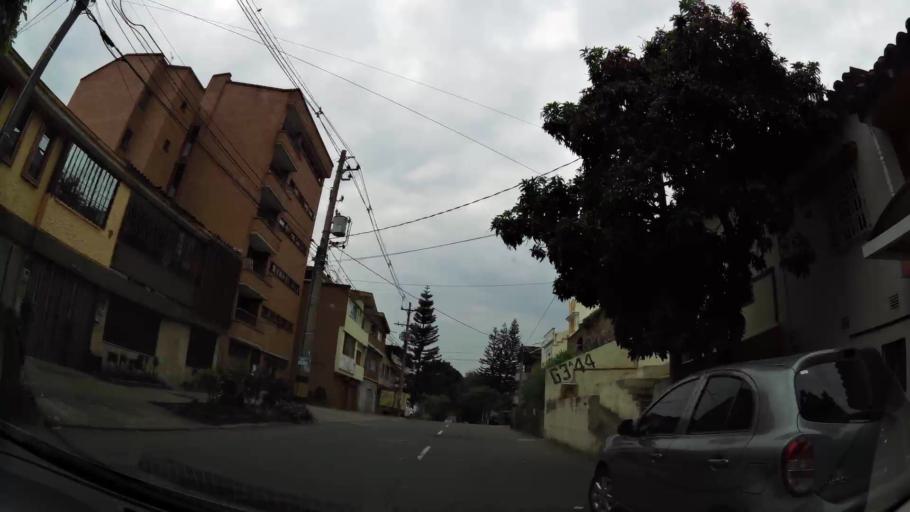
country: CO
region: Antioquia
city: Medellin
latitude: 6.2602
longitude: -75.5605
